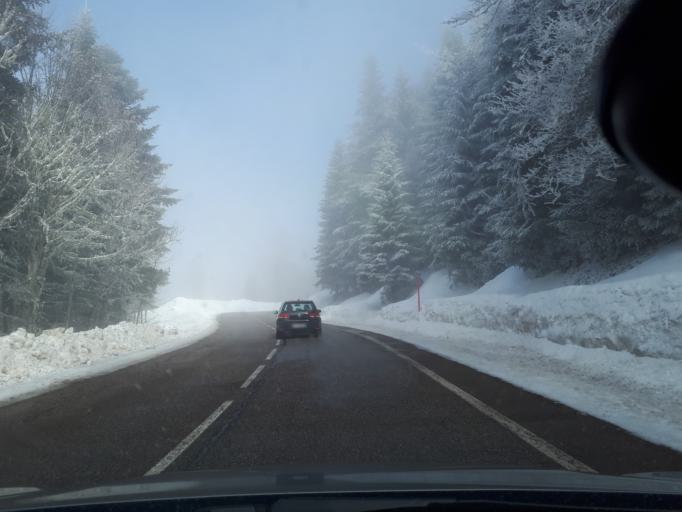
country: FR
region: Rhone-Alpes
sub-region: Departement de l'Isere
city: Vaulnaveys-le-Bas
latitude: 45.1012
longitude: 5.8591
